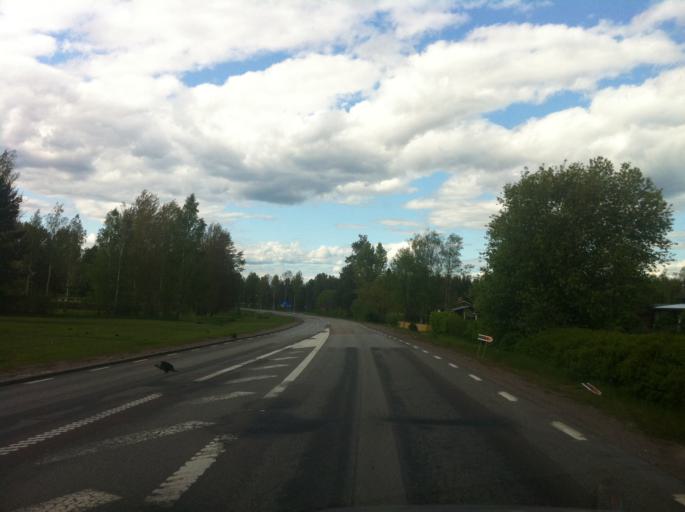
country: SE
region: Vaermland
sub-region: Storfors Kommun
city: Storfors
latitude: 59.5302
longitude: 14.2832
